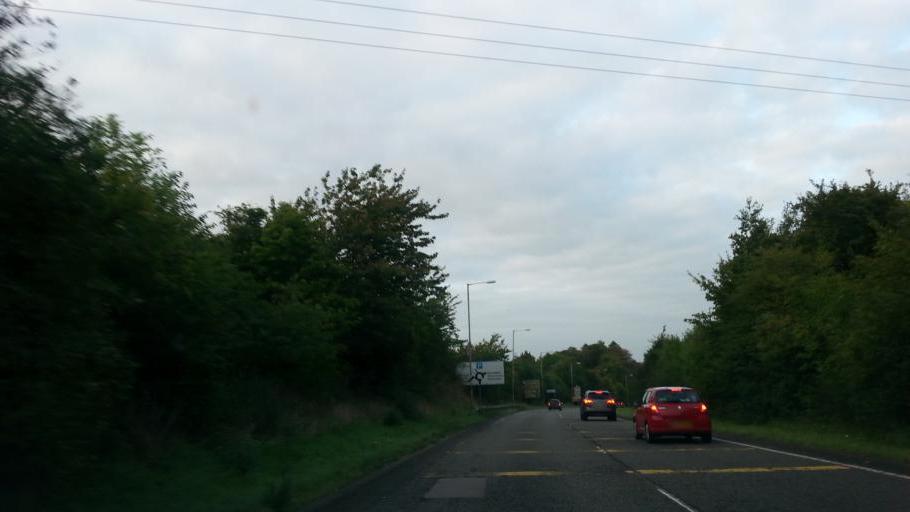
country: GB
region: England
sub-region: Northamptonshire
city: Brackley
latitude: 52.0186
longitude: -1.1520
